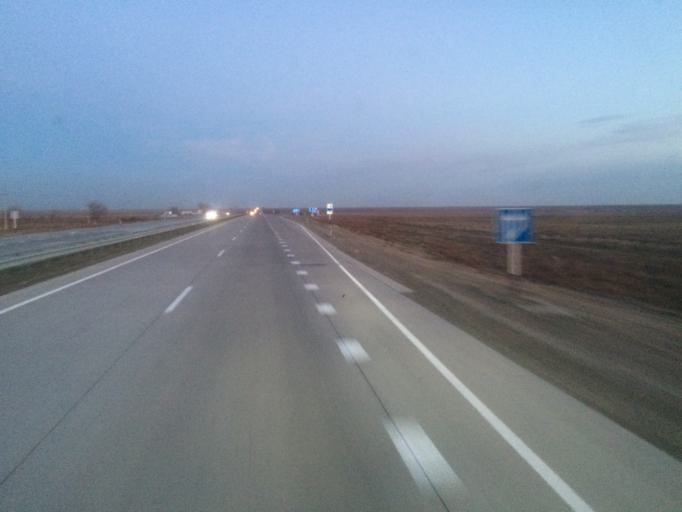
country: KZ
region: Ongtustik Qazaqstan
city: Temirlanovka
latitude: 42.8470
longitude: 69.0914
